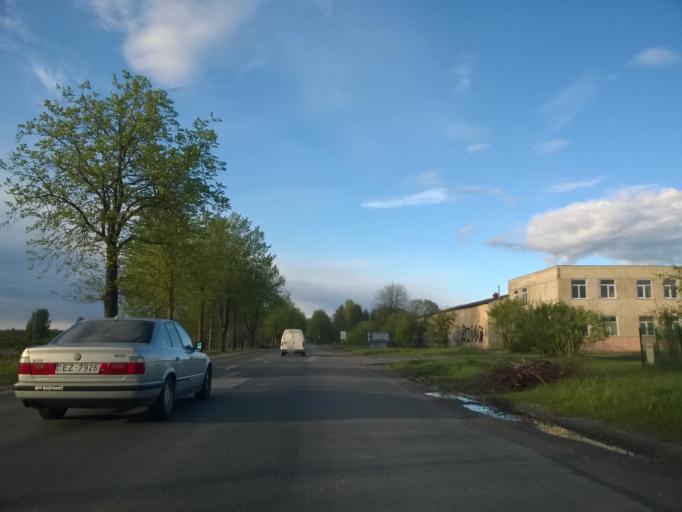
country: LV
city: Tireli
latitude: 56.9394
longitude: 23.6010
